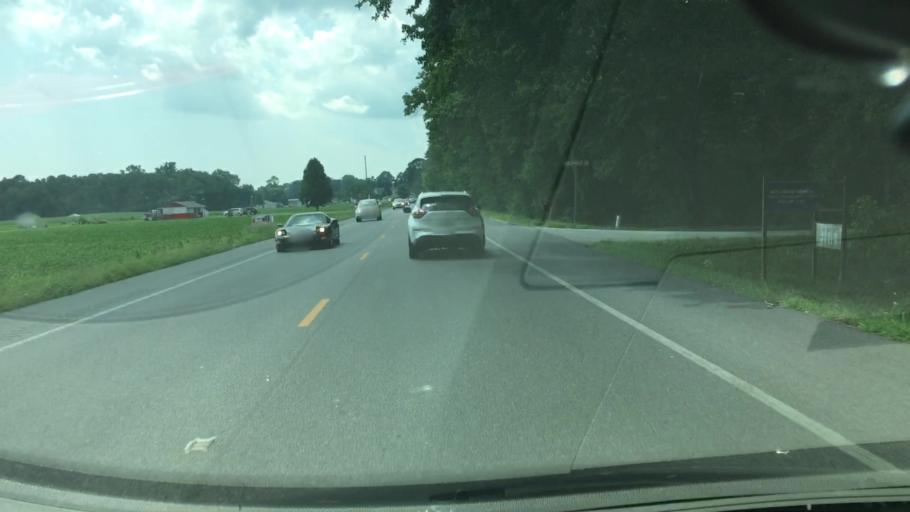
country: US
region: Maryland
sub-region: Worcester County
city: Ocean Pines
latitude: 38.3662
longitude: -75.1660
